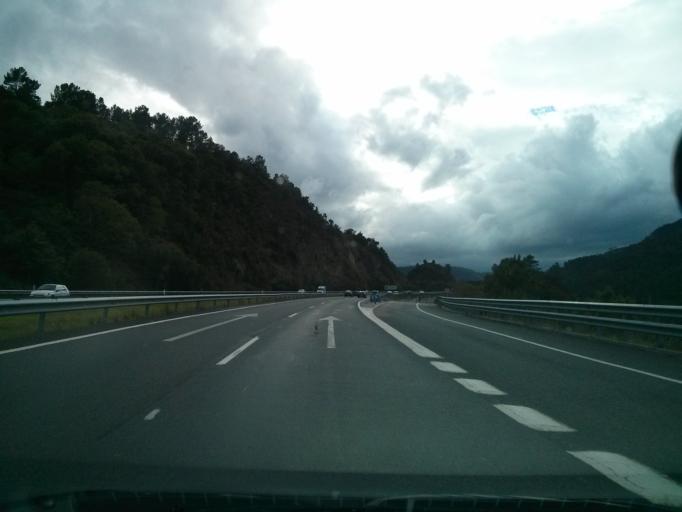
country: ES
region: Galicia
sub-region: Provincia de Ourense
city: Toen
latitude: 42.3454
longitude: -7.9158
